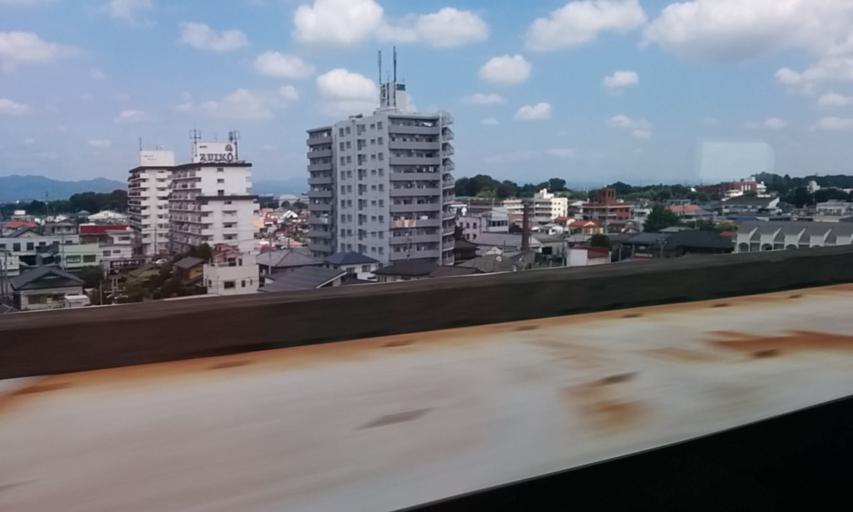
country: JP
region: Tochigi
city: Oyama
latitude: 36.3063
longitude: 139.8021
